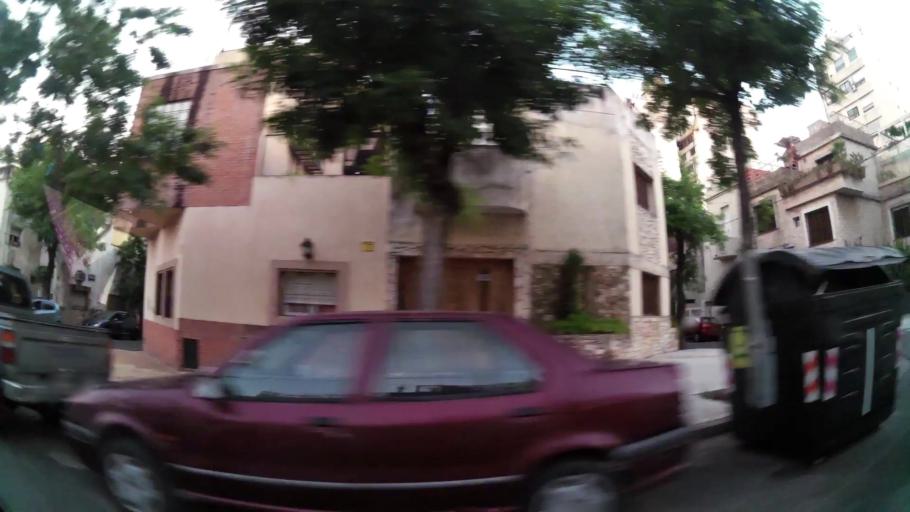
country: AR
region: Buenos Aires F.D.
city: Villa Santa Rita
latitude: -34.6323
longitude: -58.4403
